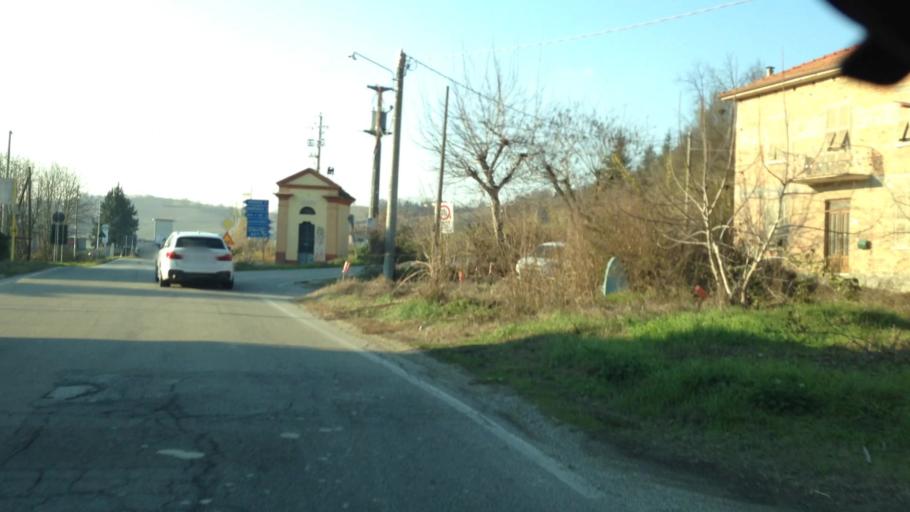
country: IT
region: Piedmont
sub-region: Provincia di Asti
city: Cortiglione
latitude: 44.8322
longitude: 8.3563
